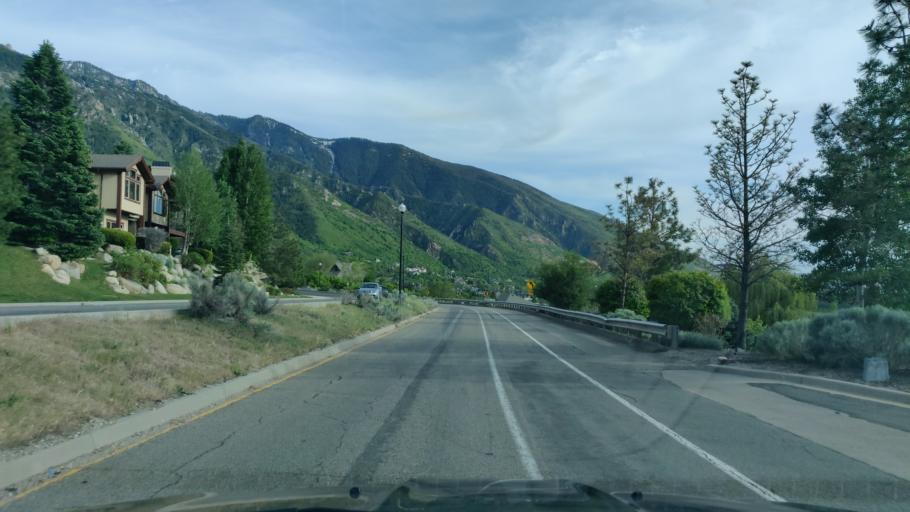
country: US
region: Utah
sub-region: Salt Lake County
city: Granite
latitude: 40.5635
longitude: -111.8041
